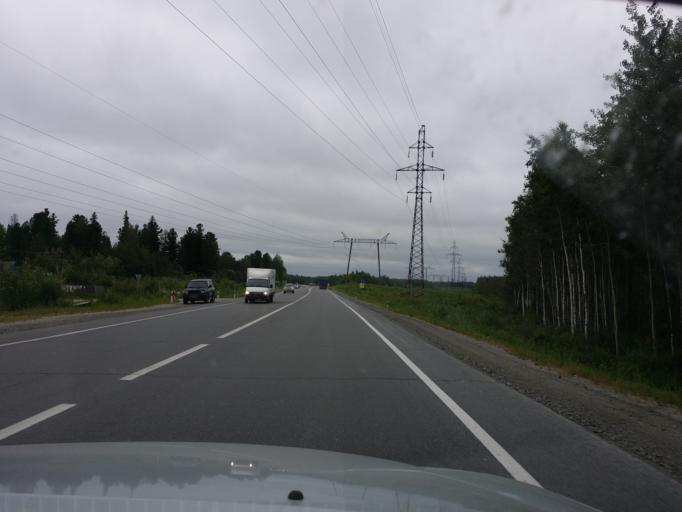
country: RU
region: Khanty-Mansiyskiy Avtonomnyy Okrug
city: Nizhnevartovsk
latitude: 61.0446
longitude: 76.3485
